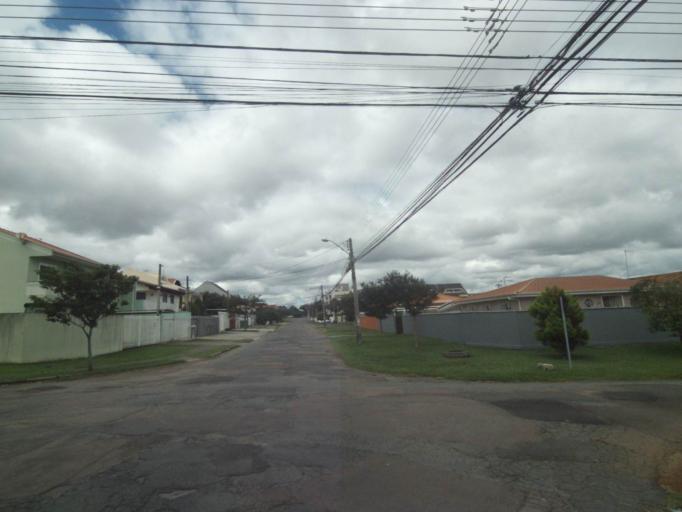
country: BR
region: Parana
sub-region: Curitiba
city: Curitiba
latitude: -25.4841
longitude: -49.2746
